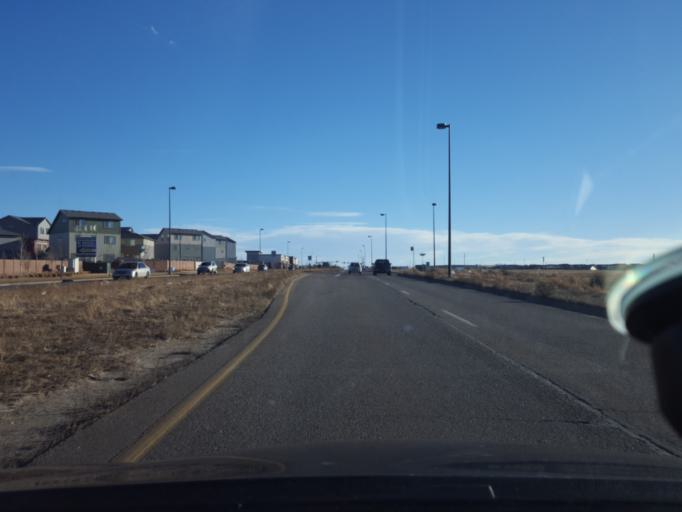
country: US
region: Colorado
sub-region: Adams County
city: Aurora
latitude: 39.7906
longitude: -104.7722
